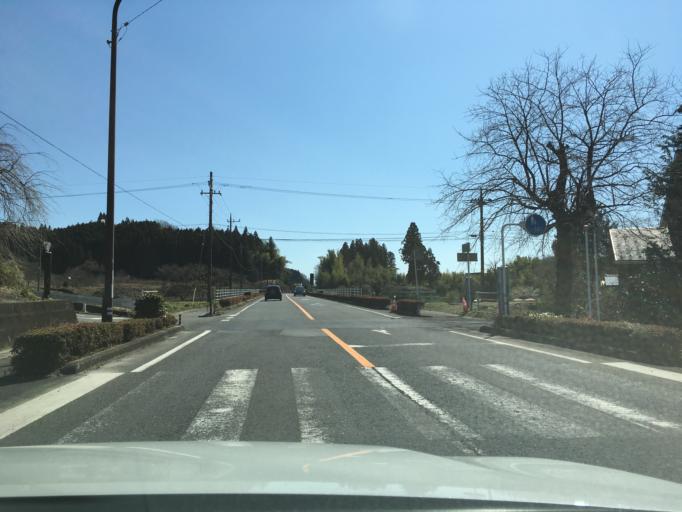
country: JP
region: Tochigi
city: Kuroiso
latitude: 37.0406
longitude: 140.1710
